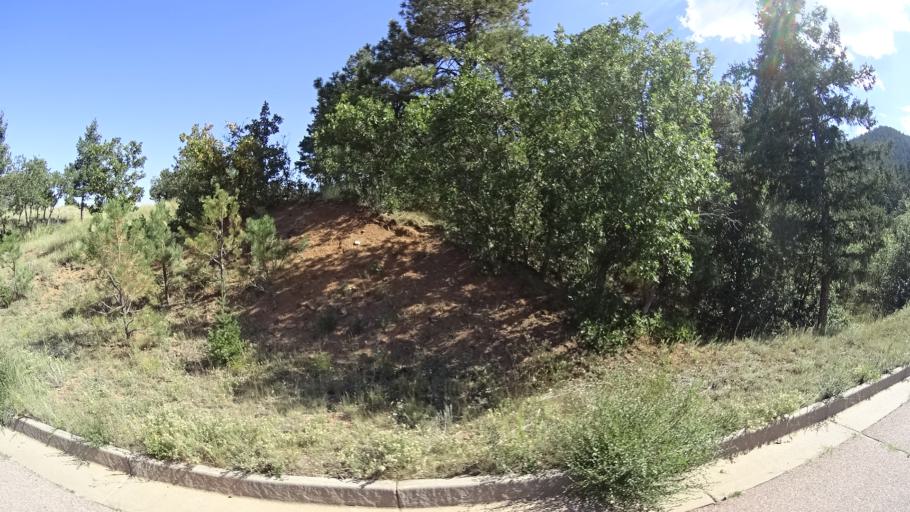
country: US
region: Colorado
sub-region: El Paso County
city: Manitou Springs
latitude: 38.8140
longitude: -104.8802
